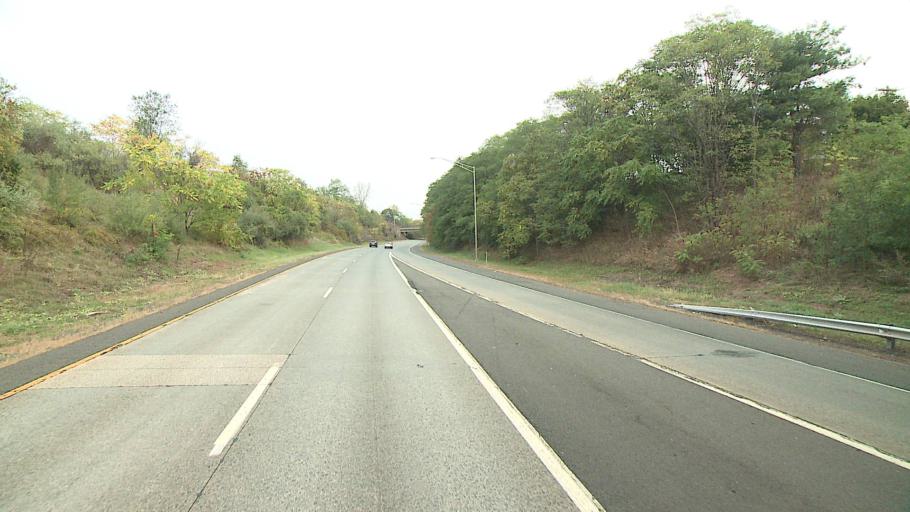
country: US
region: Connecticut
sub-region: Hartford County
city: New Britain
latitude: 41.6686
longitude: -72.7730
